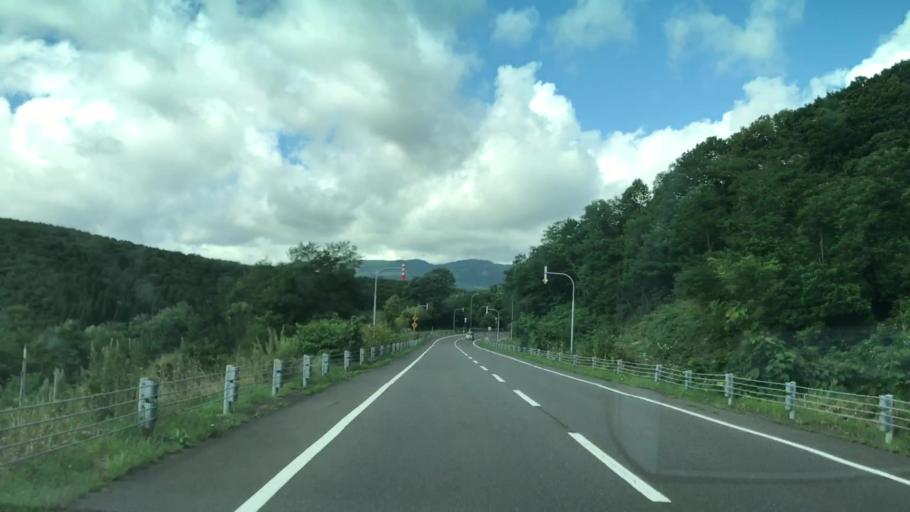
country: JP
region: Hokkaido
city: Muroran
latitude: 42.3738
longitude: 140.9617
